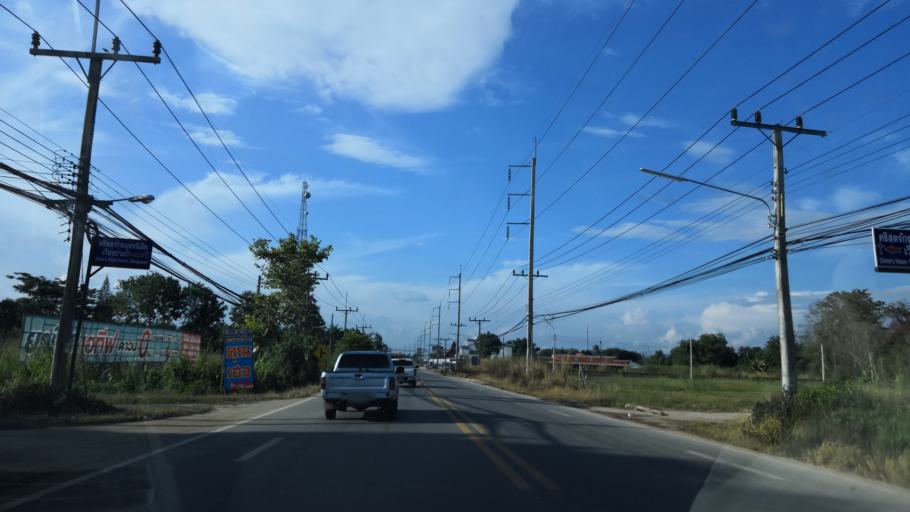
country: TH
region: Chiang Rai
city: Wiang Pa Pao
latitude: 19.3410
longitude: 99.5096
